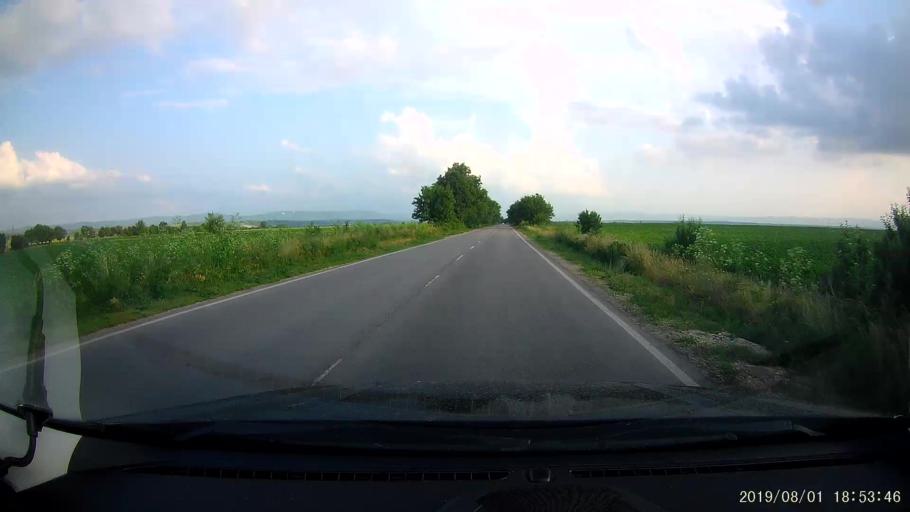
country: BG
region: Shumen
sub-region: Obshtina Shumen
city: Shumen
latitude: 43.2150
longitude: 26.9976
